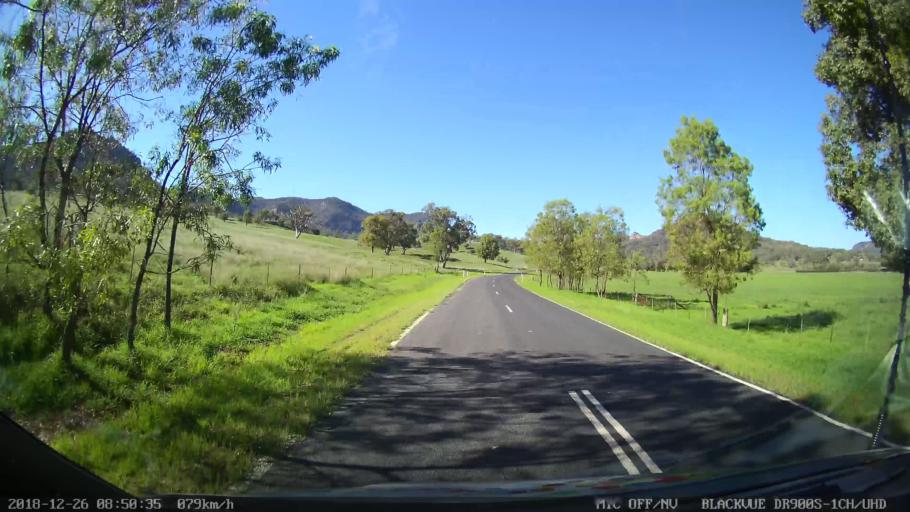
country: AU
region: New South Wales
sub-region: Mid-Western Regional
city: Kandos
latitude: -32.5770
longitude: 150.0946
